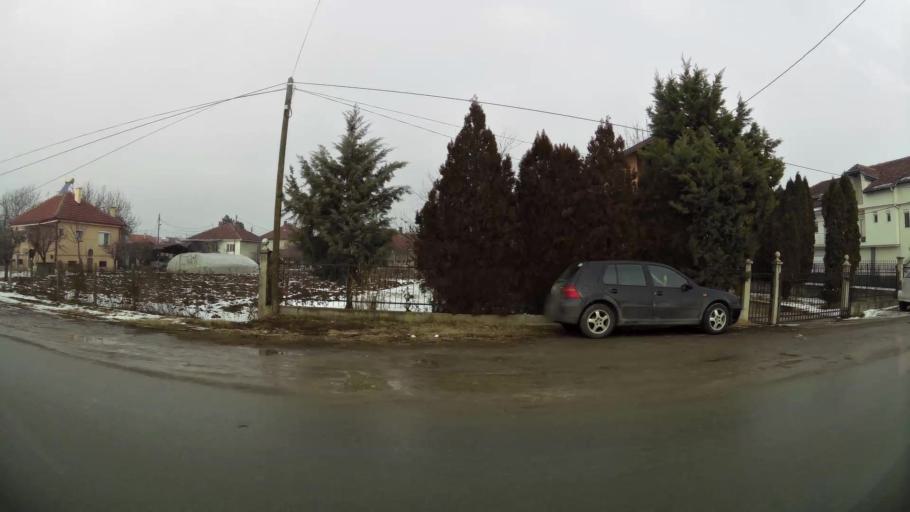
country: MK
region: Ilinden
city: Ilinden
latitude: 41.9958
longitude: 21.5829
